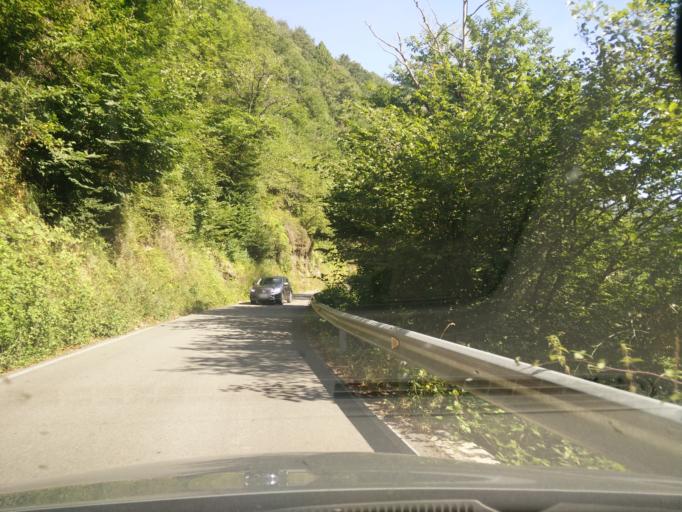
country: ES
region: Asturias
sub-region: Province of Asturias
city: Campo de Caso
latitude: 43.1786
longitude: -5.3905
